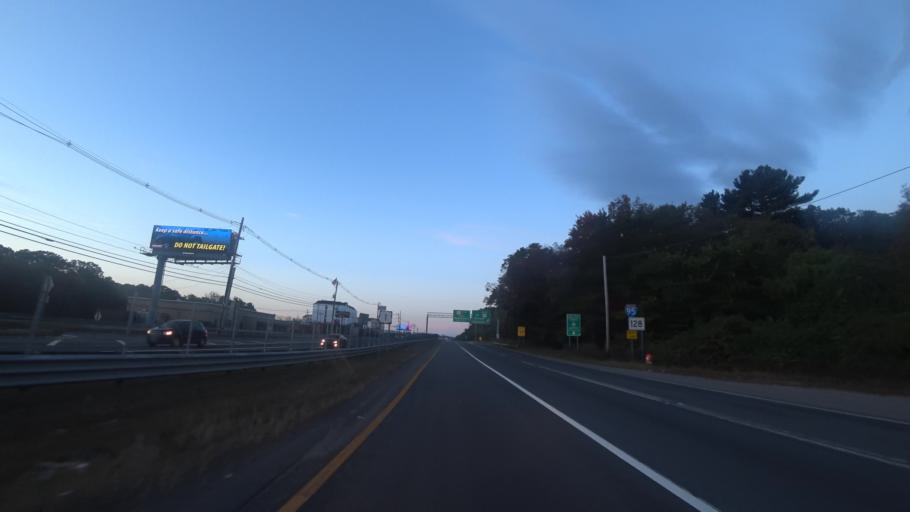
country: US
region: Massachusetts
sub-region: Essex County
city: South Peabody
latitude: 42.5288
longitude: -70.9934
